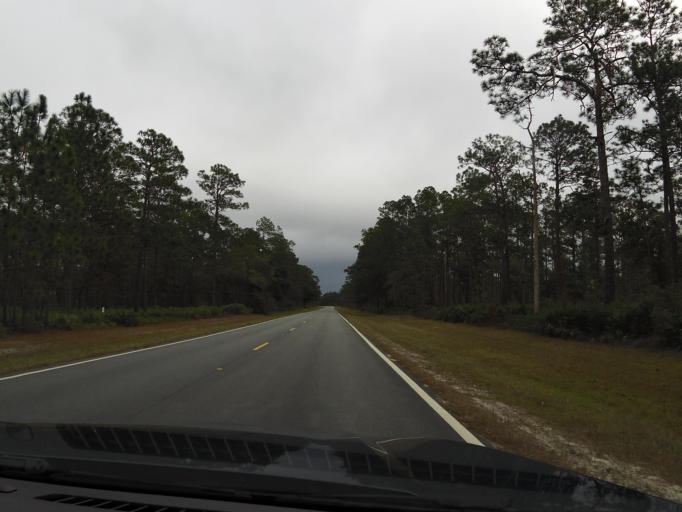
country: US
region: Georgia
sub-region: Charlton County
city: Folkston
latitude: 30.7410
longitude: -82.1242
